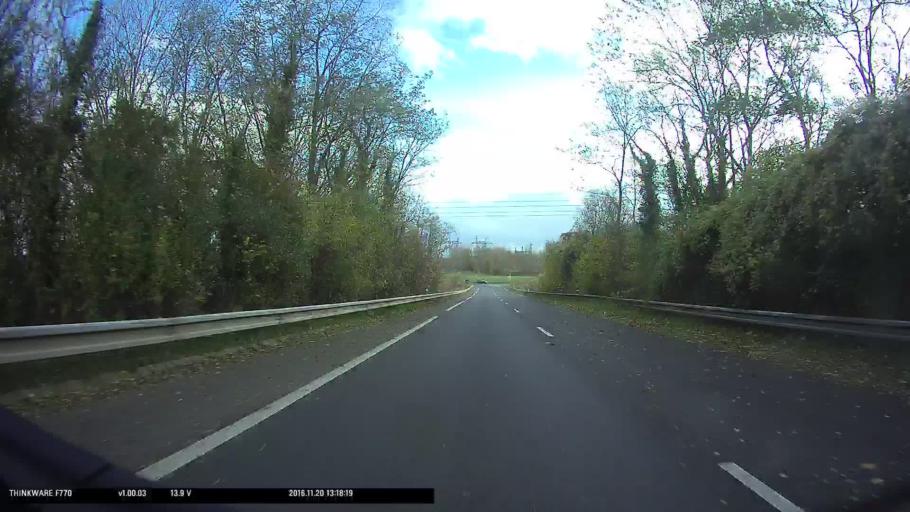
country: FR
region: Ile-de-France
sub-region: Departement du Val-d'Oise
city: Courdimanche
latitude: 49.0574
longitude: 2.0084
